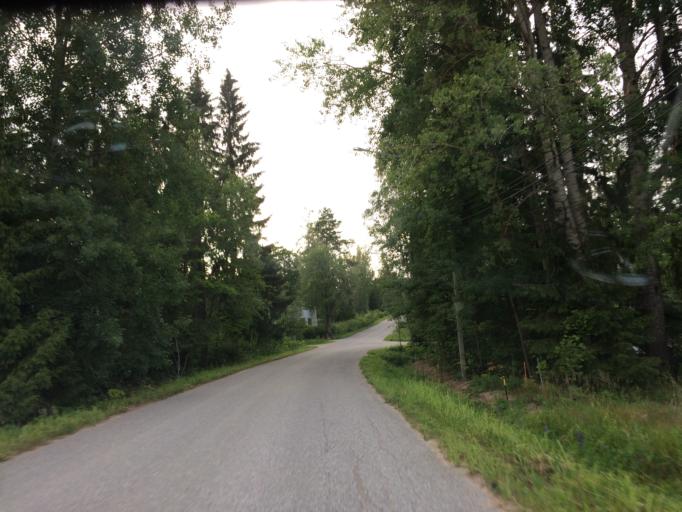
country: FI
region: Haeme
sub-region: Haemeenlinna
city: Tervakoski
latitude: 60.8499
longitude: 24.6219
